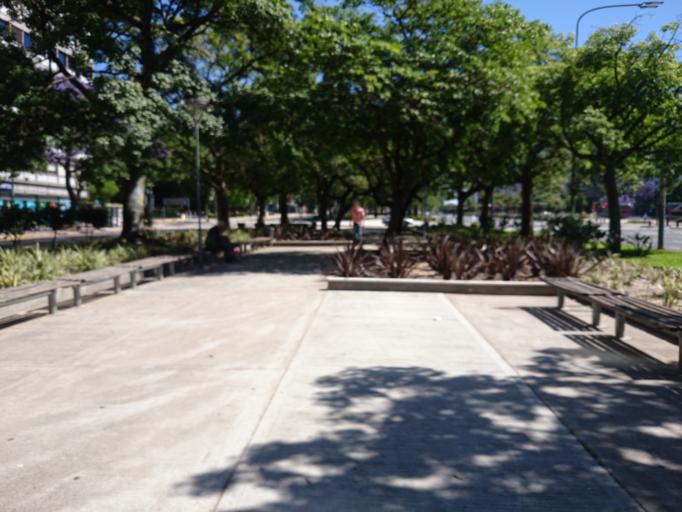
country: AR
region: Buenos Aires F.D.
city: Retiro
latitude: -34.5985
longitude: -58.3823
